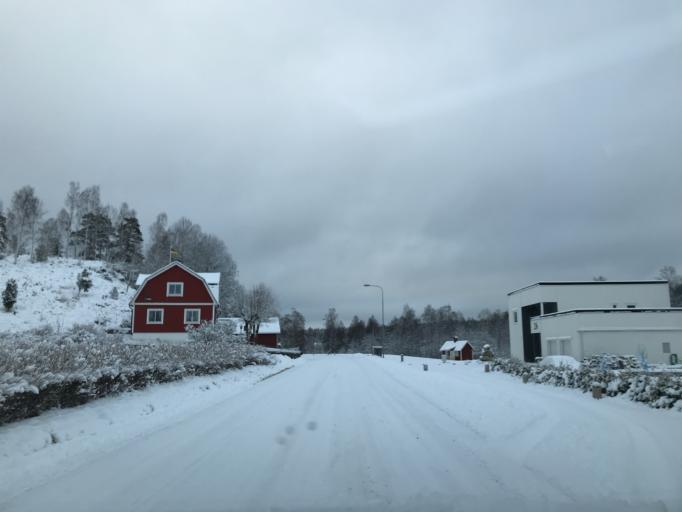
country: SE
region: Vaestra Goetaland
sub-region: Bollebygds Kommun
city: Bollebygd
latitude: 57.7952
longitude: 12.6431
